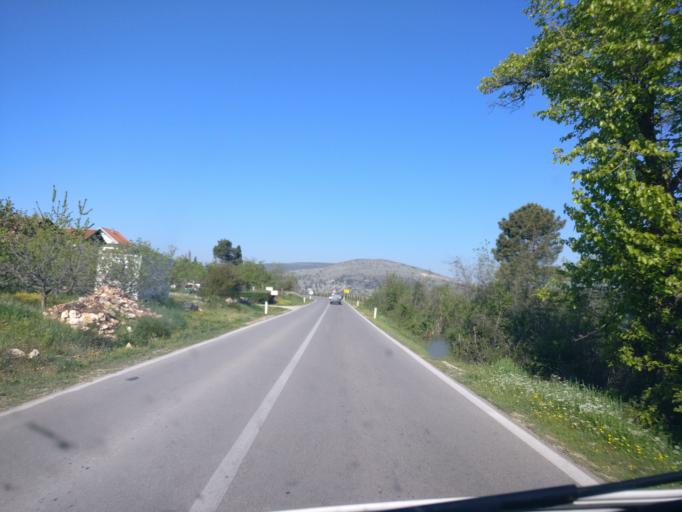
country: BA
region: Federation of Bosnia and Herzegovina
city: Tasovcici
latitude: 43.1197
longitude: 17.7332
